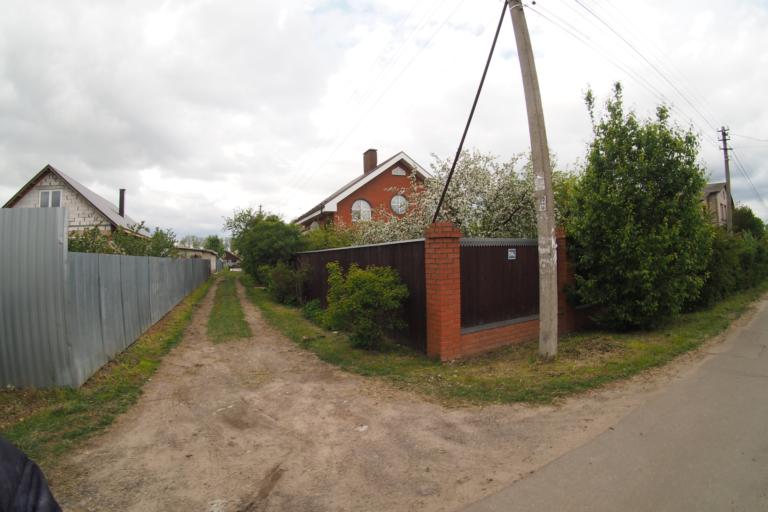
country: RU
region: Moskovskaya
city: Rechitsy
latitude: 55.5795
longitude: 38.5034
